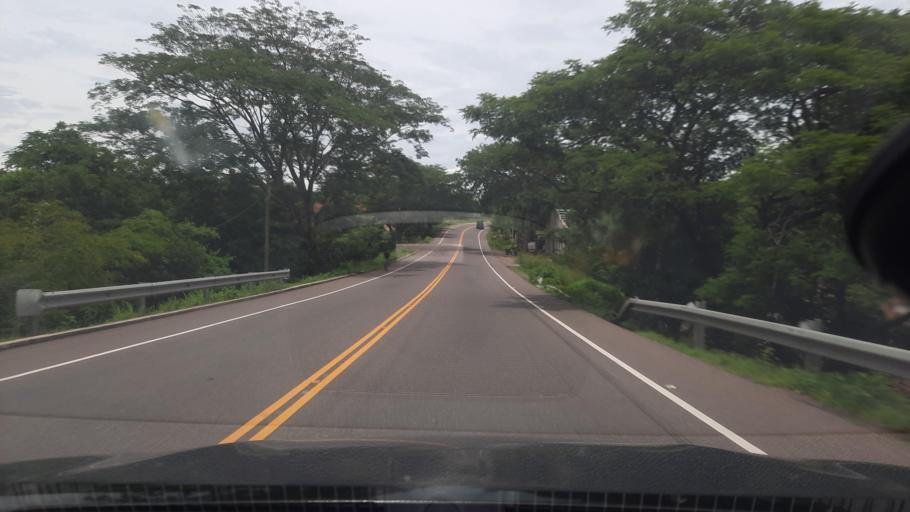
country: HN
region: Valle
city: Langue
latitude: 13.5788
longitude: -87.6836
